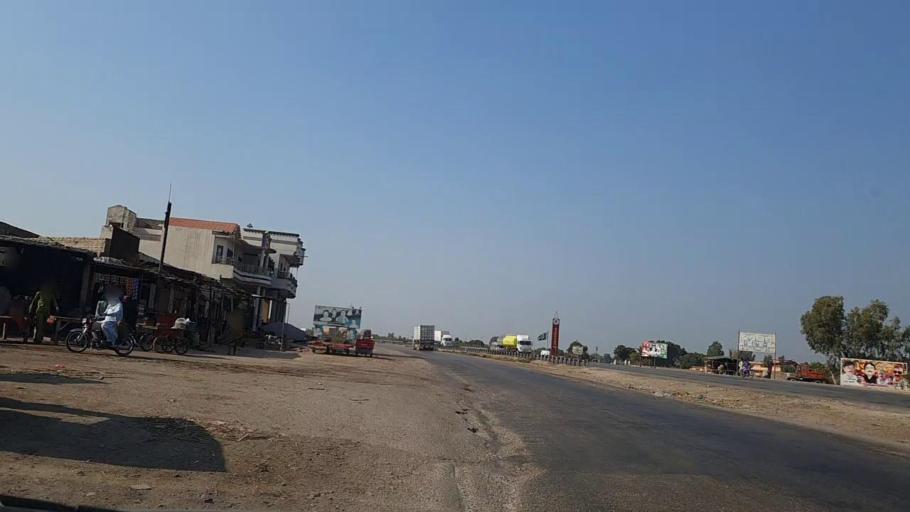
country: PK
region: Sindh
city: Sakrand
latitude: 26.1114
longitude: 68.2911
